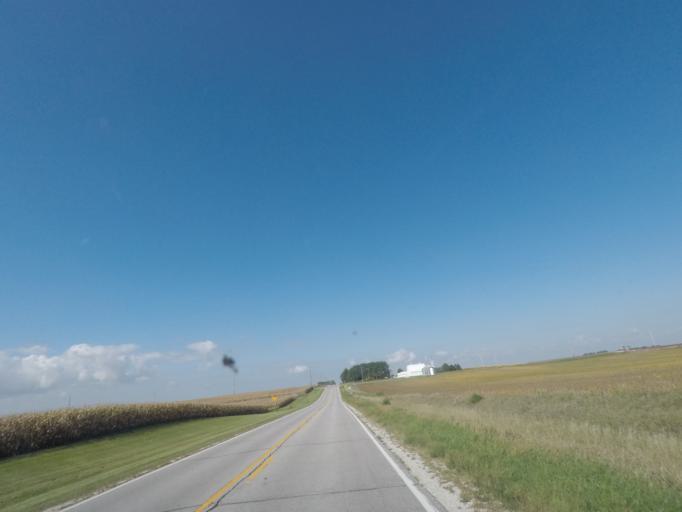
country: US
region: Iowa
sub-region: Story County
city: Nevada
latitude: 42.0226
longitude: -93.4026
